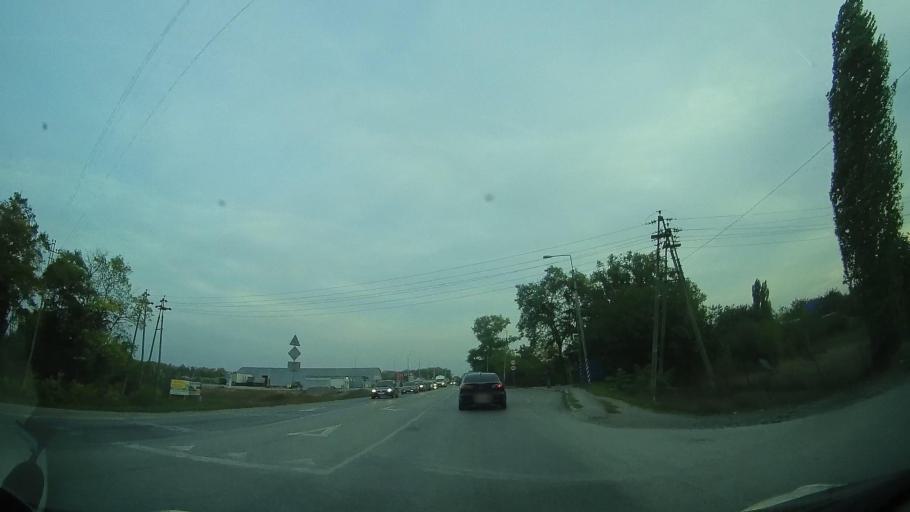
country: RU
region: Rostov
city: Kirovskaya
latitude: 46.9748
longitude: 40.0487
